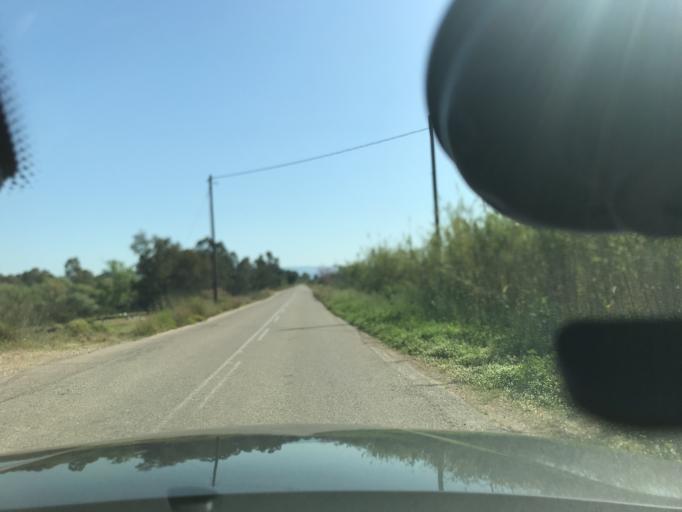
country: GR
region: West Greece
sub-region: Nomos Ileias
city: Epitalion
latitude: 37.6407
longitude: 21.4939
